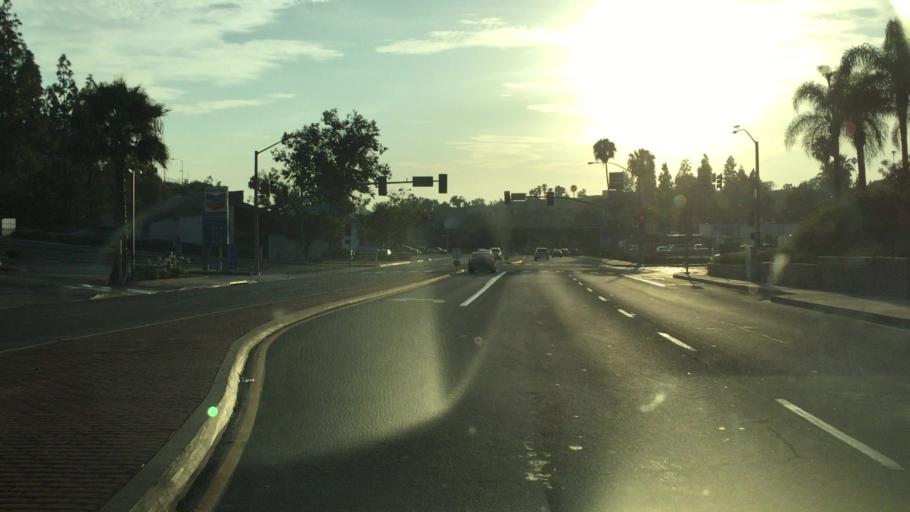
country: US
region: California
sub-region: San Diego County
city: La Mesa
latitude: 32.7764
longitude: -117.0149
